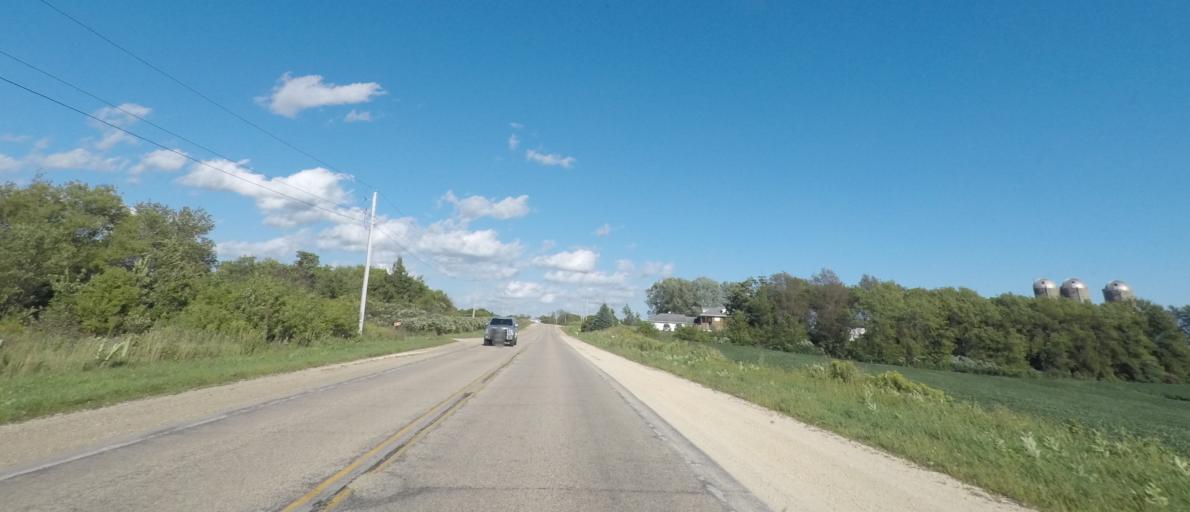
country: US
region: Wisconsin
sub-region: Iowa County
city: Dodgeville
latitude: 42.9794
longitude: -90.0660
